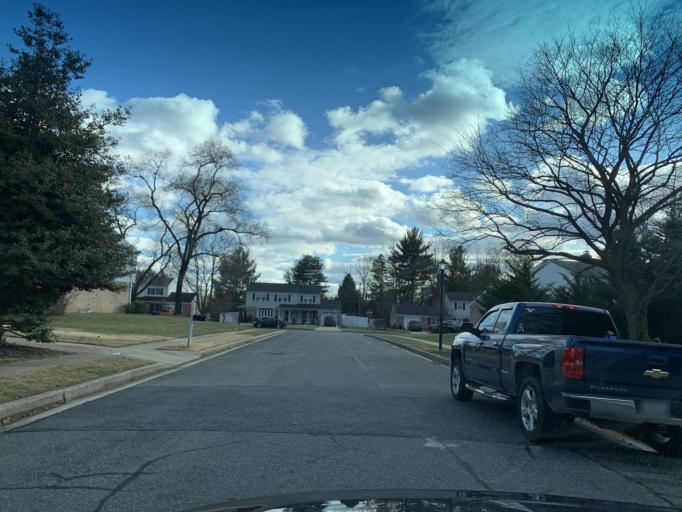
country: US
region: Maryland
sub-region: Harford County
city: South Bel Air
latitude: 39.5316
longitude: -76.3352
